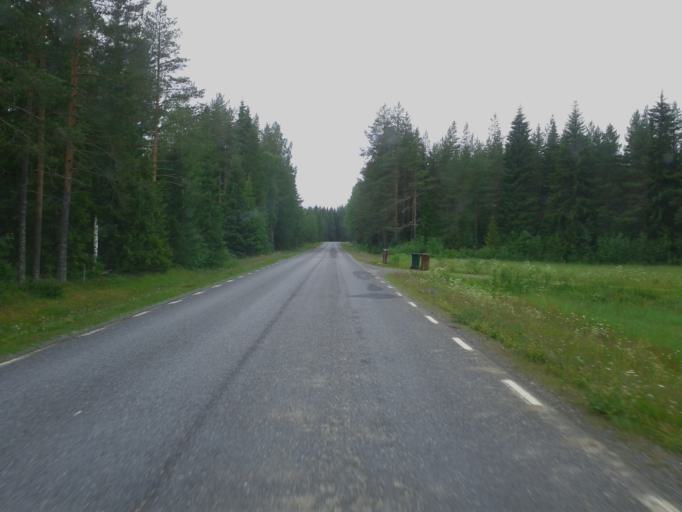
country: SE
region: Vaesterbotten
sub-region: Skelleftea Kommun
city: Forsbacka
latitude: 64.8990
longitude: 20.6729
